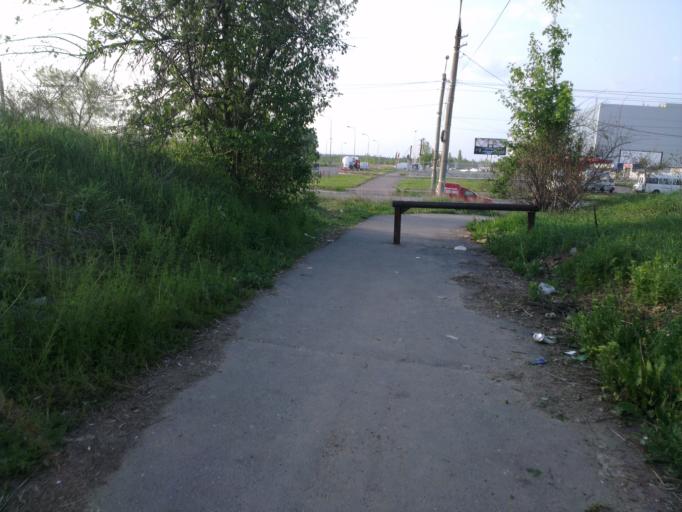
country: MD
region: Chisinau
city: Stauceni
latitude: 47.0677
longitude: 28.8872
